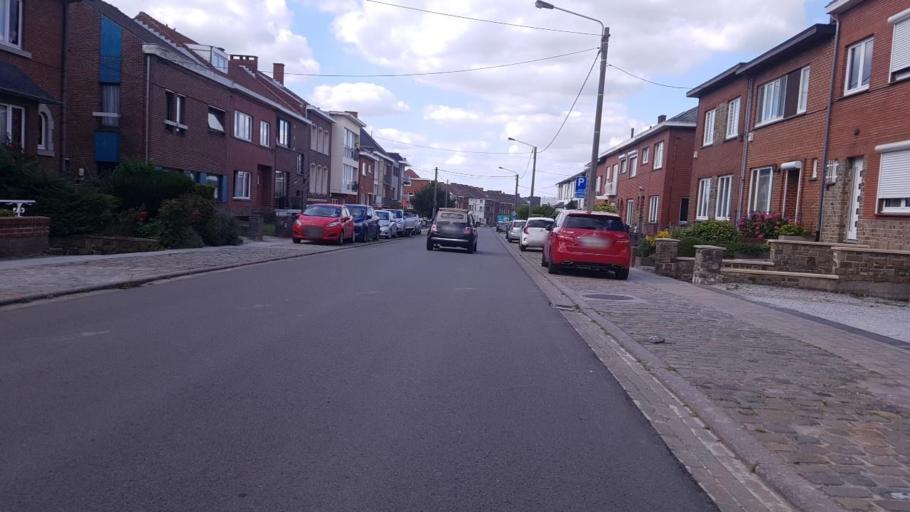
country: BE
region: Wallonia
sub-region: Province du Hainaut
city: Charleroi
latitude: 50.3888
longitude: 4.4565
